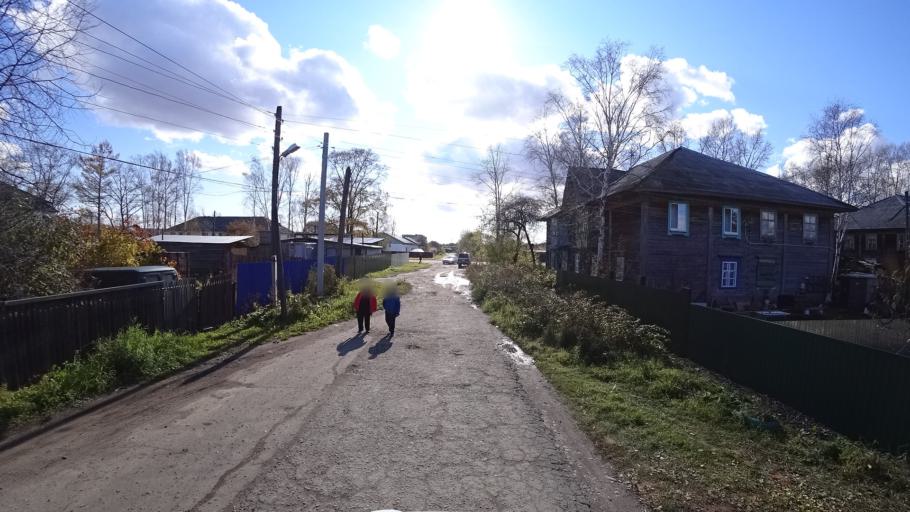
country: RU
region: Khabarovsk Krai
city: Amursk
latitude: 50.1004
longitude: 136.5004
